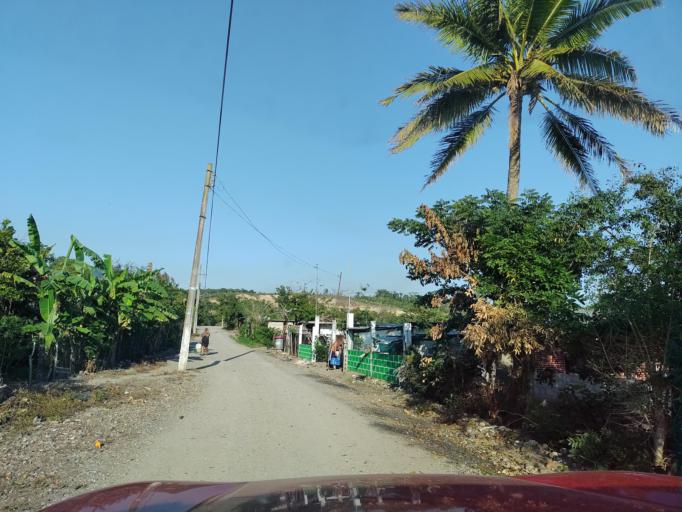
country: MX
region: Veracruz
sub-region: Papantla
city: Polutla
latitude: 20.4488
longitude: -97.2445
